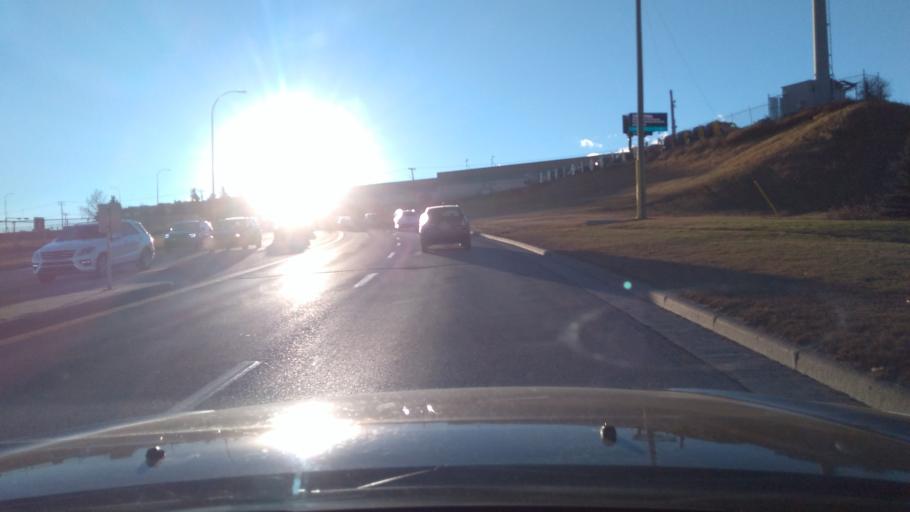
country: CA
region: Alberta
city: Calgary
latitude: 50.9869
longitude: -114.0462
